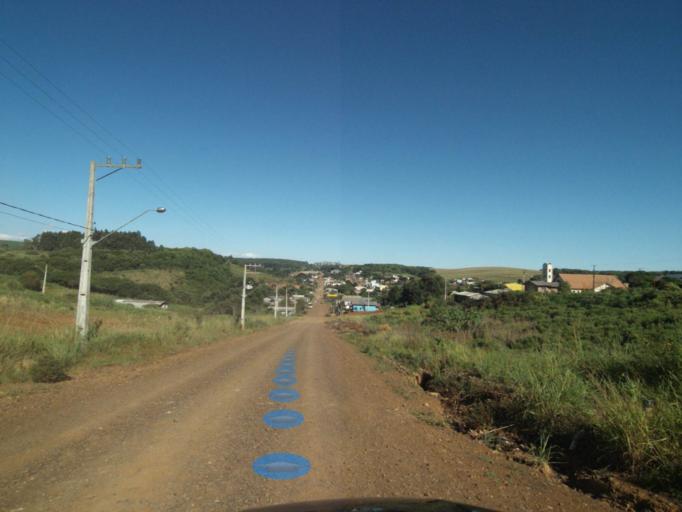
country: BR
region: Parana
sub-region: Coronel Vivida
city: Coronel Vivida
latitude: -26.1406
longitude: -52.3901
